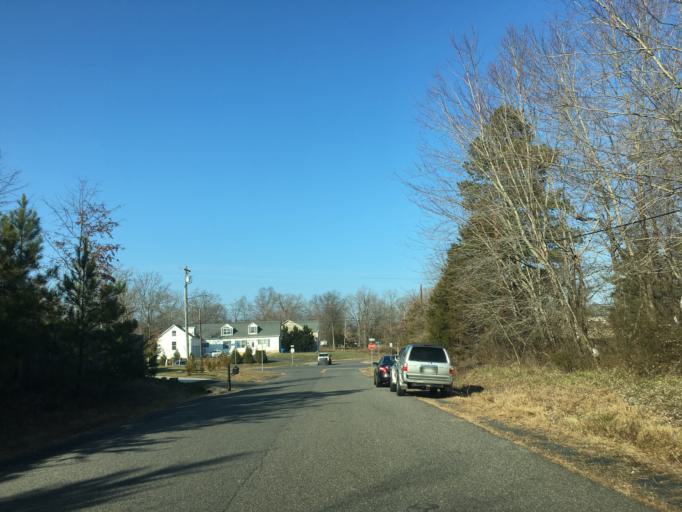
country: US
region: Virginia
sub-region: Fairfax County
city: Fairfax Station
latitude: 38.8262
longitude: -77.3717
